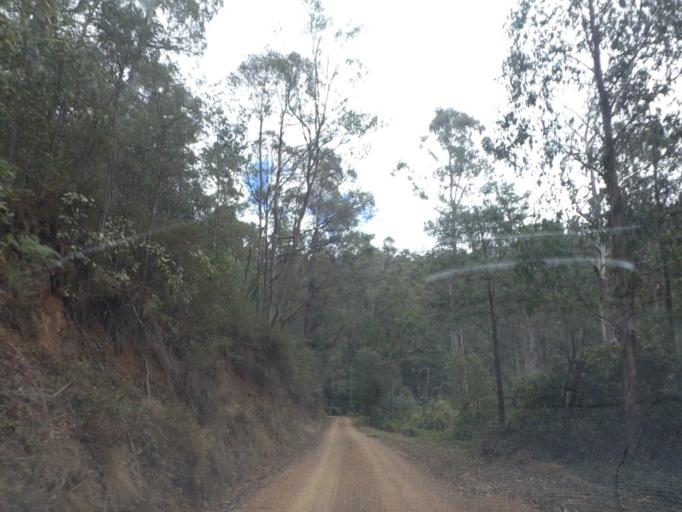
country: AU
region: Victoria
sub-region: Murrindindi
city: Alexandra
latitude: -37.4338
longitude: 145.9667
